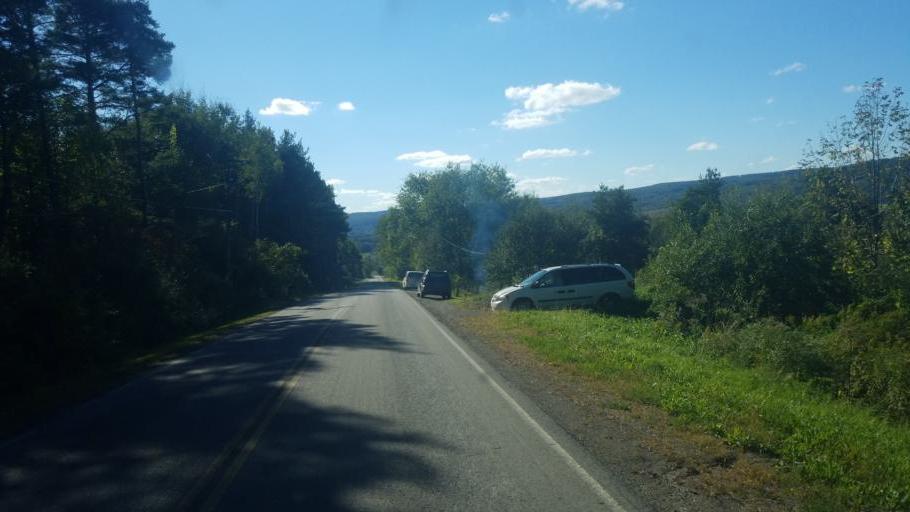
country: US
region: New York
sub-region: Allegany County
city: Friendship
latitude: 42.2766
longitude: -78.1883
